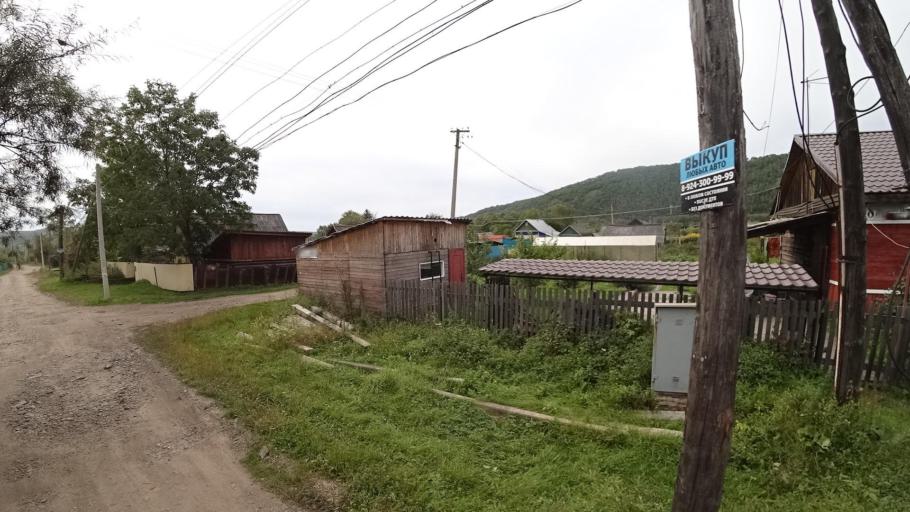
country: RU
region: Jewish Autonomous Oblast
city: Khingansk
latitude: 48.9951
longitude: 131.0549
